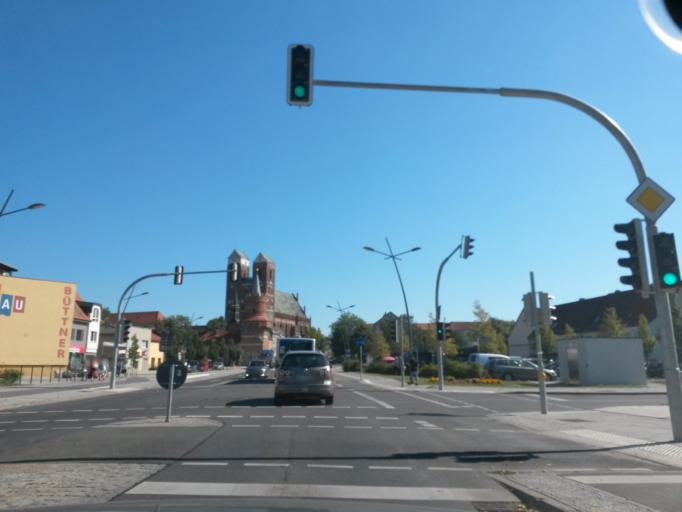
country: DE
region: Brandenburg
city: Prenzlau
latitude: 53.3117
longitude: 13.8521
